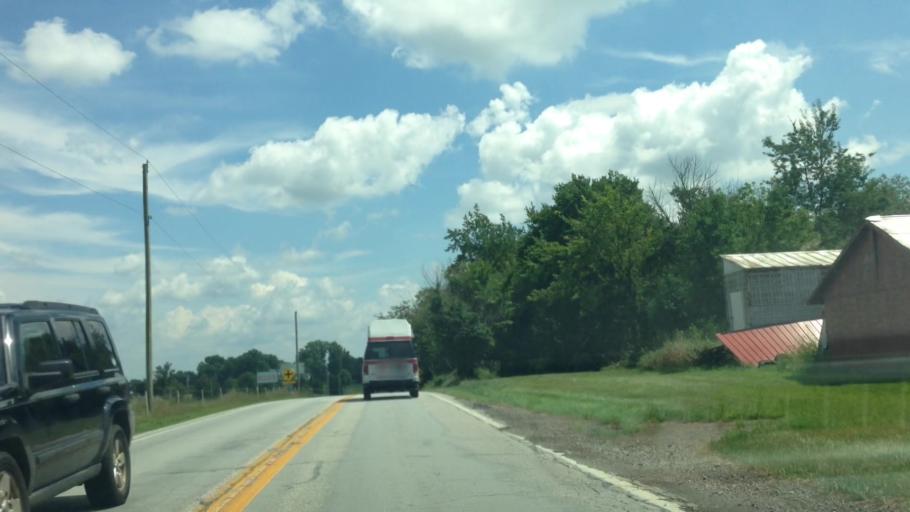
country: US
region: Ohio
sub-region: Wayne County
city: Rittman
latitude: 40.9165
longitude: -81.7873
